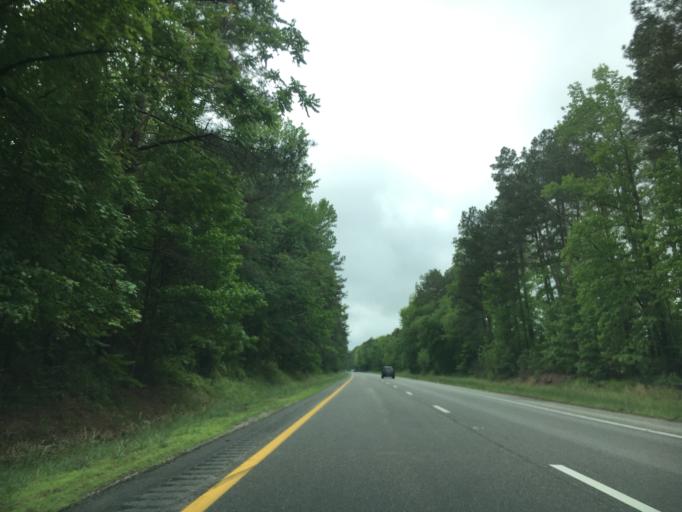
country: US
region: Virginia
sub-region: Brunswick County
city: Lawrenceville
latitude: 36.9039
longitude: -77.7906
